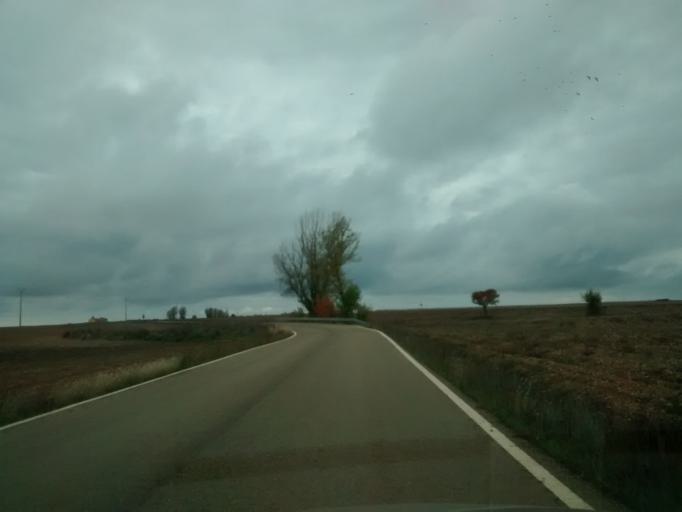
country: ES
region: Aragon
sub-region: Provincia de Zaragoza
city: Torralba de los Frailes
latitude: 41.0425
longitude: -1.6406
